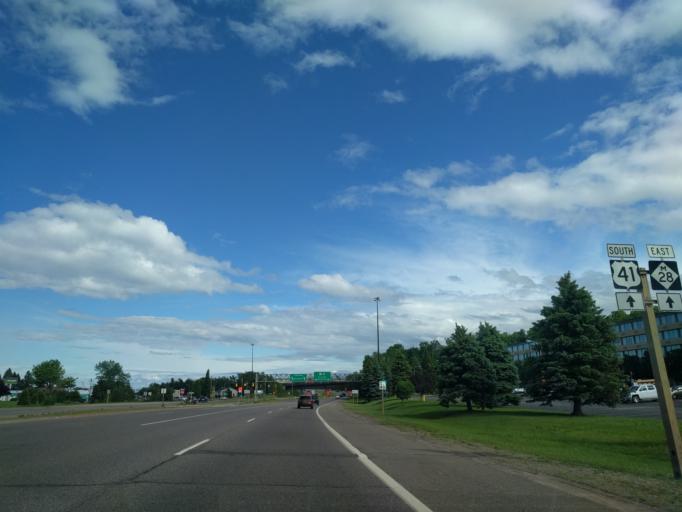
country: US
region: Michigan
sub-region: Marquette County
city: Trowbridge Park
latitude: 46.5471
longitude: -87.4304
